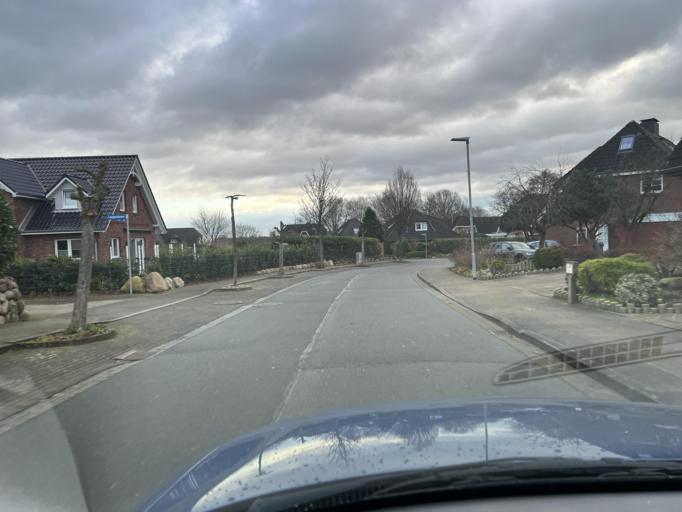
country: DE
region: Schleswig-Holstein
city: Ostrohe
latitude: 54.2009
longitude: 9.1267
